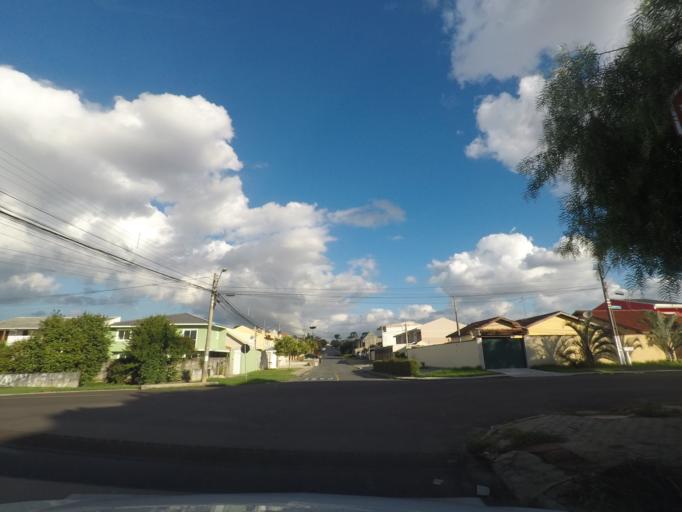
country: BR
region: Parana
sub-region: Sao Jose Dos Pinhais
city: Sao Jose dos Pinhais
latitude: -25.4952
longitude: -49.2559
